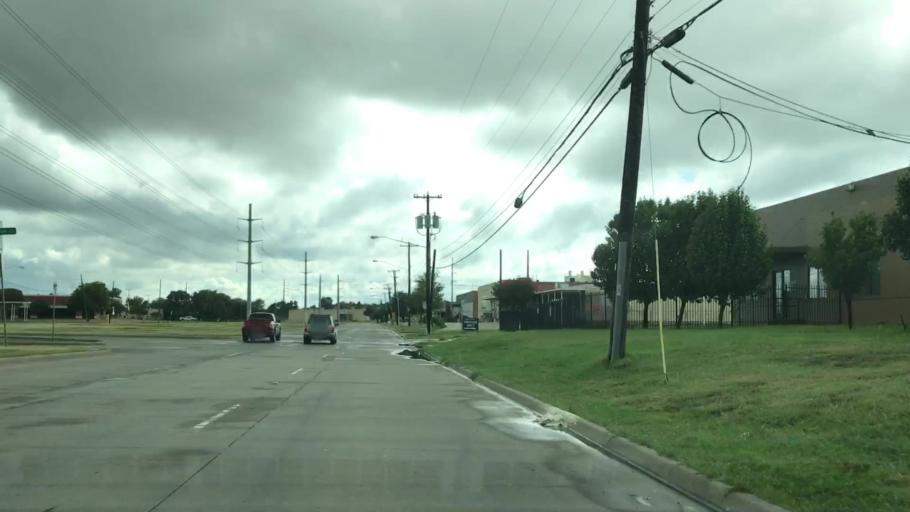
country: US
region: Texas
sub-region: Dallas County
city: Irving
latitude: 32.8190
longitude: -96.8968
